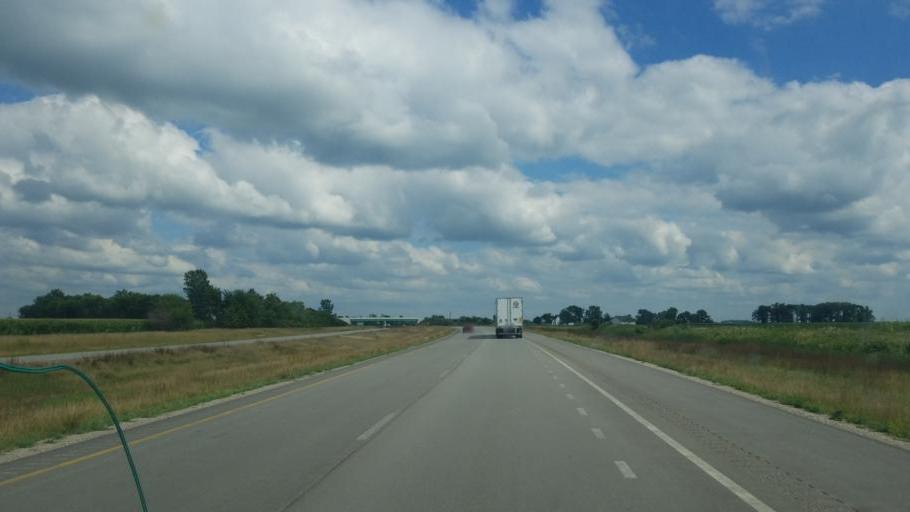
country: US
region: Ohio
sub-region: Van Wert County
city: Van Wert
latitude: 40.8742
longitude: -84.5200
